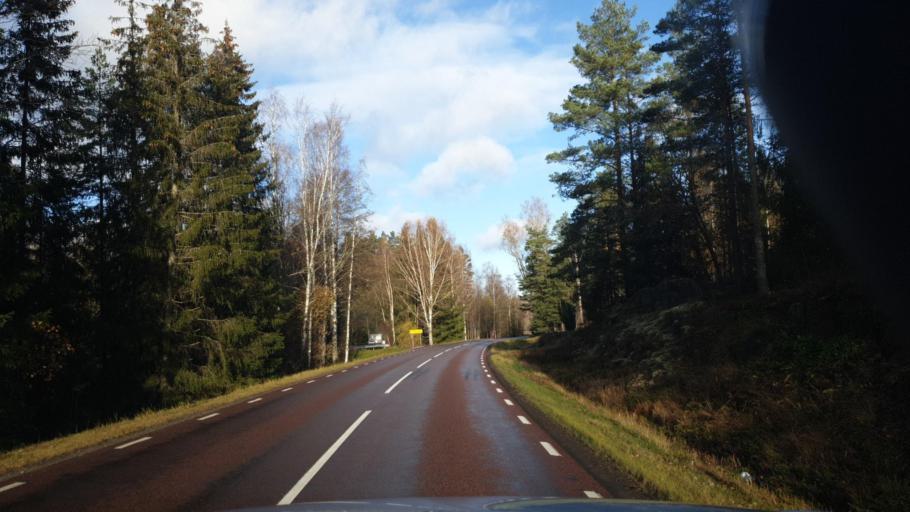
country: SE
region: Vaermland
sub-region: Grums Kommun
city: Slottsbron
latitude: 59.4199
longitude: 12.9822
